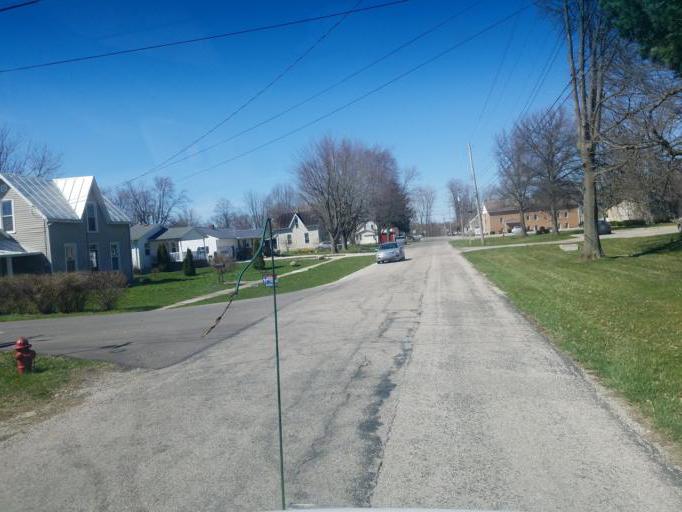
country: US
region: Ohio
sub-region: Morrow County
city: Cardington
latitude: 40.4987
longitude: -82.9017
